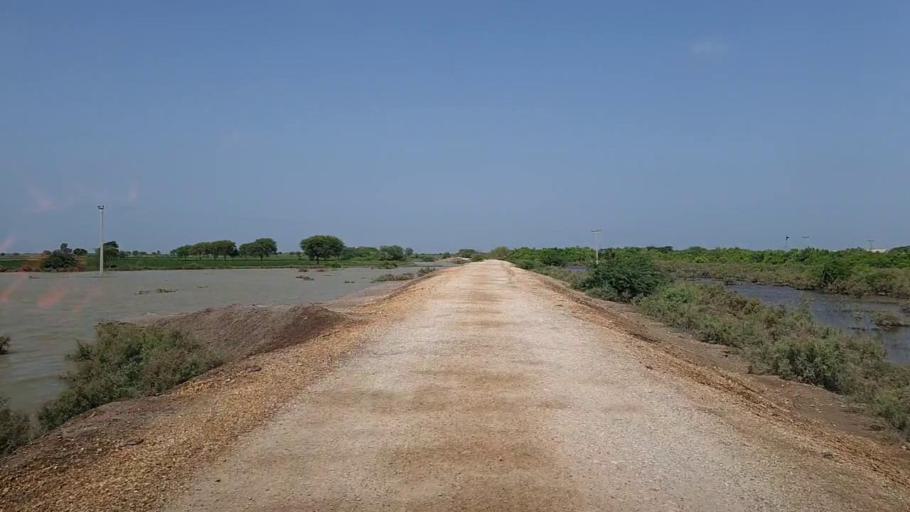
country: PK
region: Sindh
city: Mirpur Batoro
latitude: 24.6465
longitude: 68.4298
